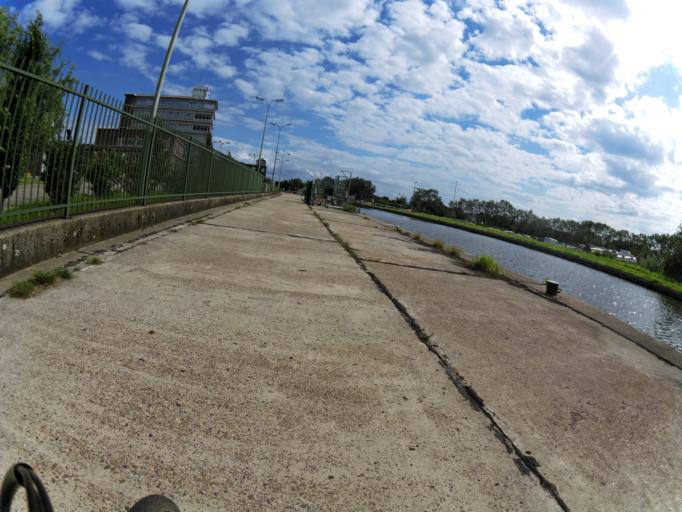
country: BE
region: Flanders
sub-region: Provincie Antwerpen
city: Balen
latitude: 51.1980
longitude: 5.2294
